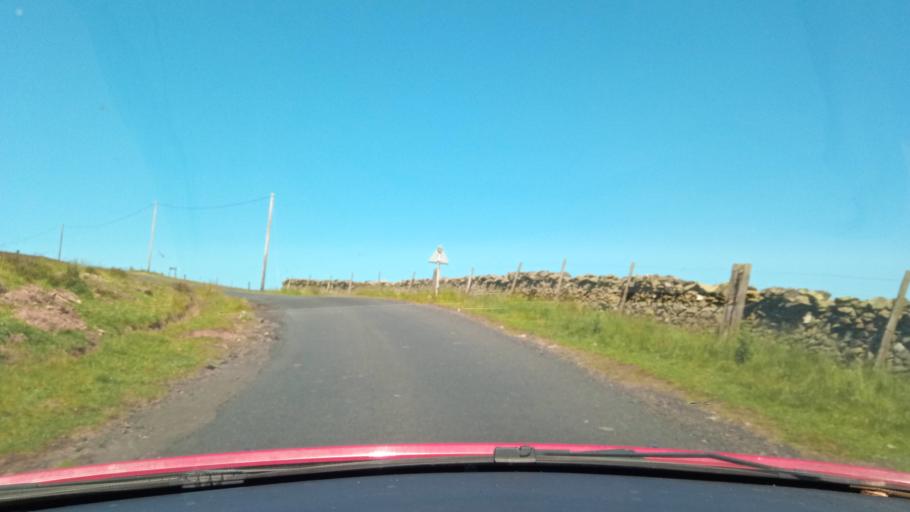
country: GB
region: Scotland
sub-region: The Scottish Borders
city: Duns
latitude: 55.8220
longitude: -2.5084
